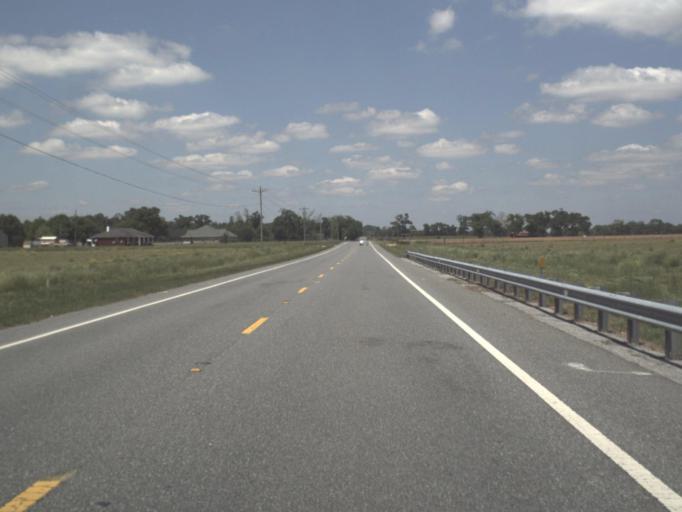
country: US
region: Florida
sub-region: Santa Rosa County
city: Point Baker
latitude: 30.8180
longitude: -87.0456
